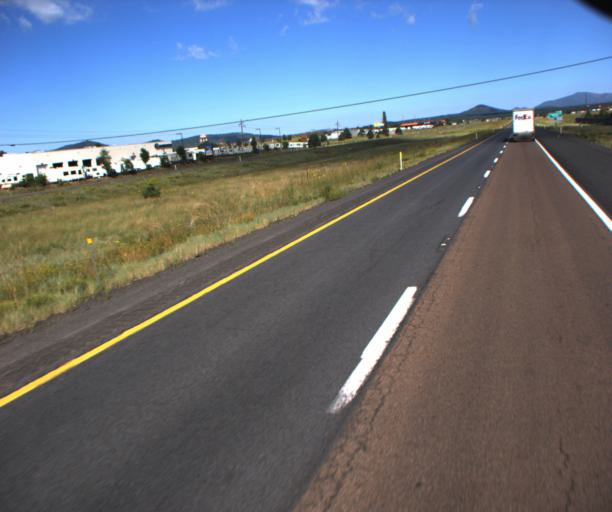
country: US
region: Arizona
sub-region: Coconino County
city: Parks
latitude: 35.2296
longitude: -111.8078
